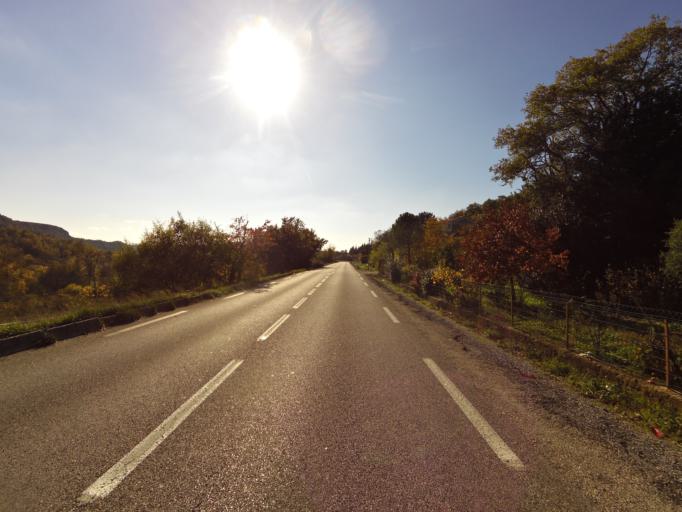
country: FR
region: Rhone-Alpes
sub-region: Departement de l'Ardeche
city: Largentiere
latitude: 44.5163
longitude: 4.3209
